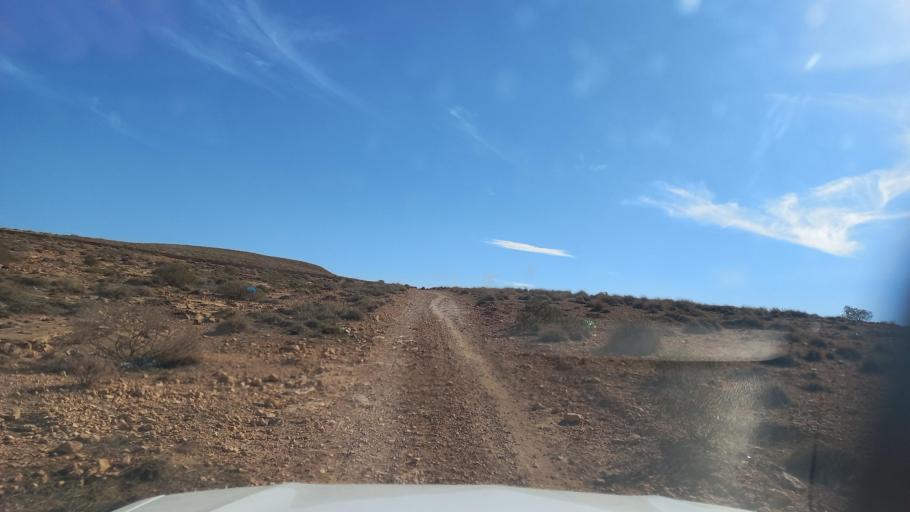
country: TN
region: Al Qasrayn
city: Kasserine
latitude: 35.2060
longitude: 8.9765
